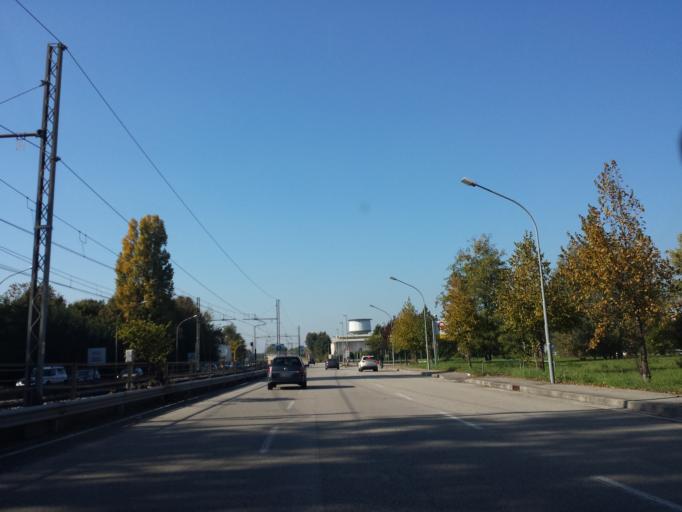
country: IT
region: Veneto
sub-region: Provincia di Padova
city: Padova
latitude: 45.4168
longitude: 11.9093
